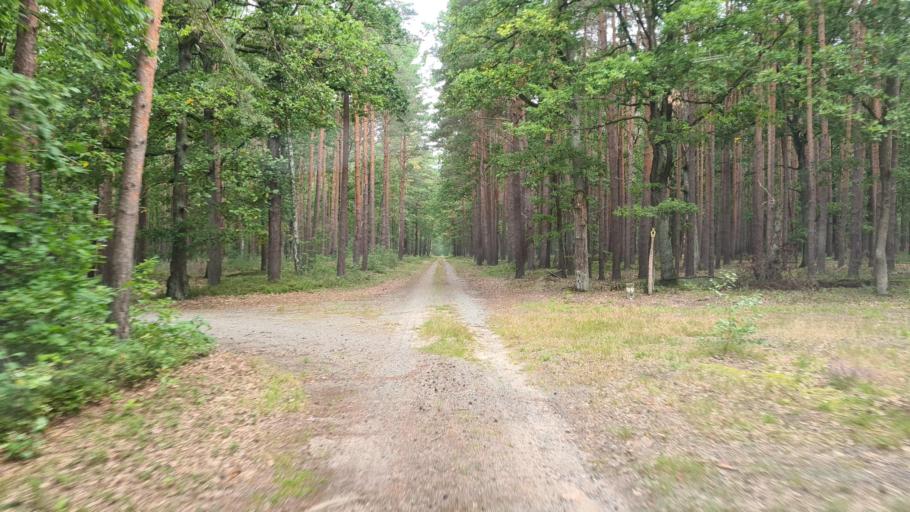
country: DE
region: Brandenburg
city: Hohenbucko
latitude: 51.7732
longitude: 13.5538
